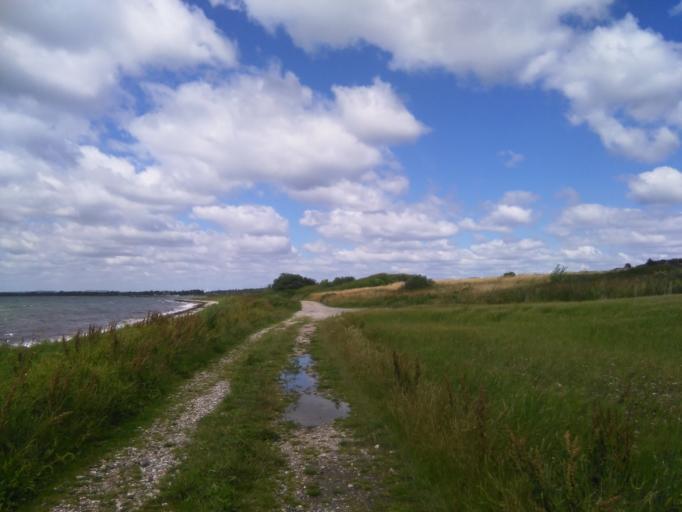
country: DK
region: Central Jutland
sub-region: Arhus Kommune
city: Logten
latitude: 56.1729
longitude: 10.3784
